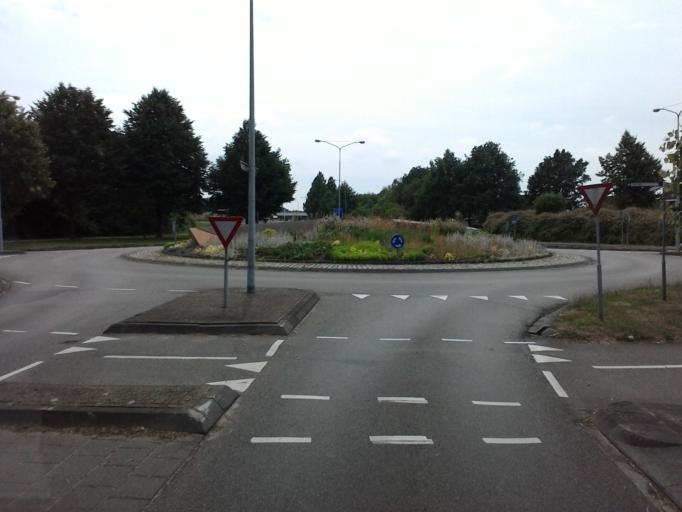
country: NL
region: Drenthe
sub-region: Gemeente Aa en Hunze
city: Anloo
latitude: 52.9785
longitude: 6.6499
